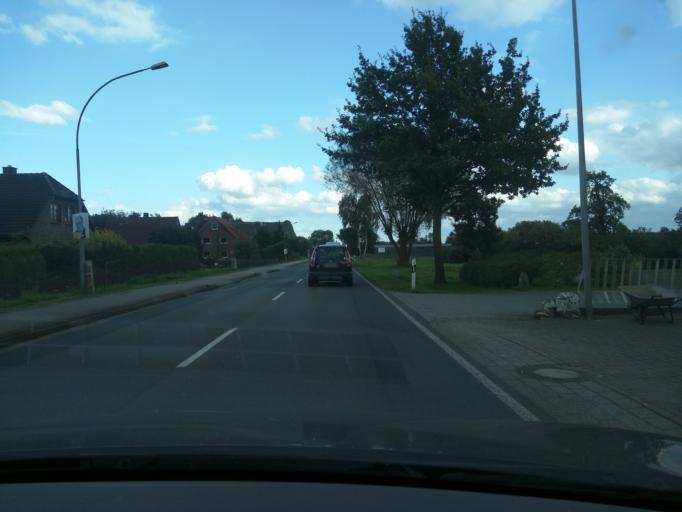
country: DE
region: Lower Saxony
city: Marschacht
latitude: 53.4183
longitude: 10.3439
